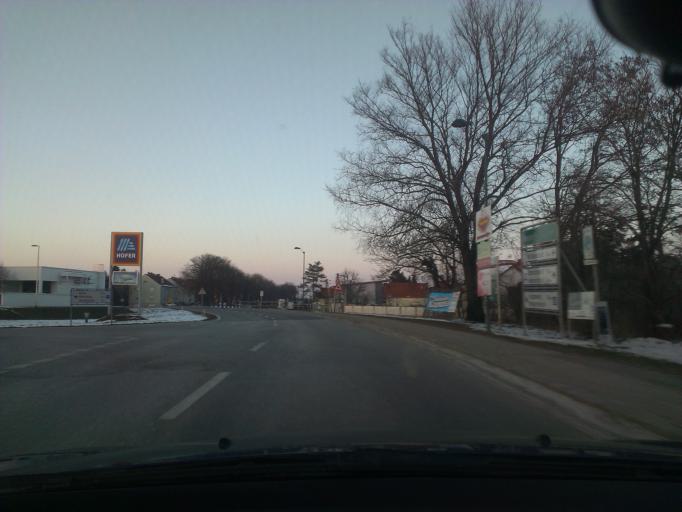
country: AT
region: Lower Austria
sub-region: Politischer Bezirk Bruck an der Leitha
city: Gotzendorf an der Leitha
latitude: 48.0155
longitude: 16.5823
